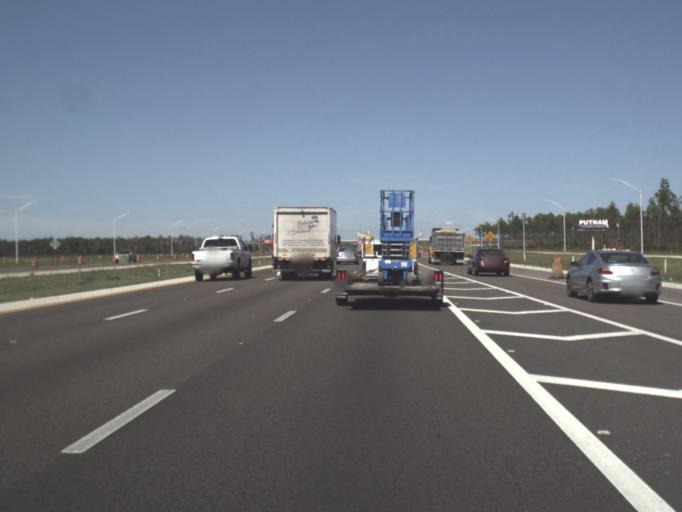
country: US
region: Florida
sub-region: Lee County
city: Three Oaks
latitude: 26.5019
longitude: -81.7943
